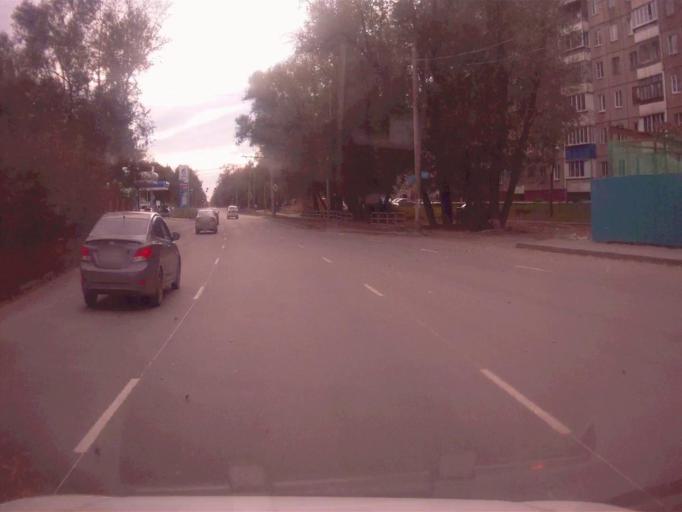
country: RU
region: Chelyabinsk
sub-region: Gorod Chelyabinsk
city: Chelyabinsk
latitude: 55.1250
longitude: 61.4752
